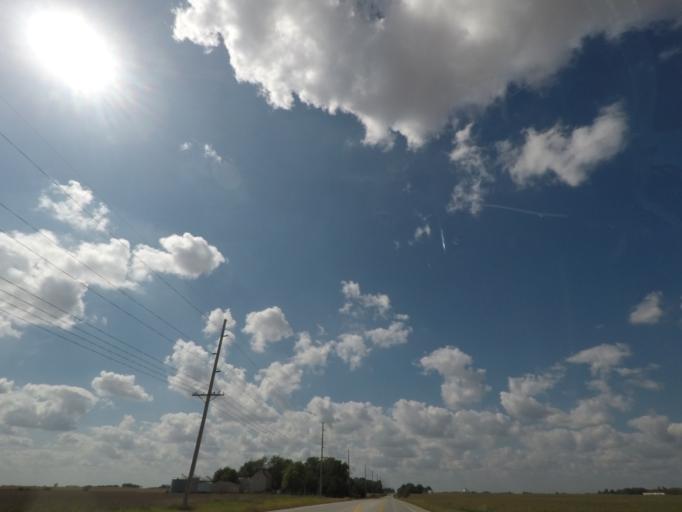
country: US
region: Iowa
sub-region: Story County
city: Nevada
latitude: 42.0231
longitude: -93.5225
